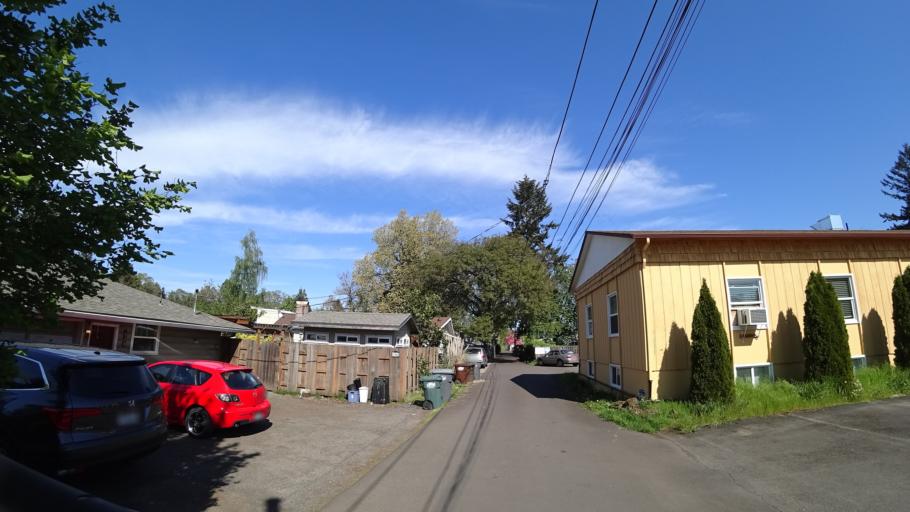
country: US
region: Oregon
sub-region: Washington County
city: Hillsboro
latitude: 45.5290
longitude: -122.9894
